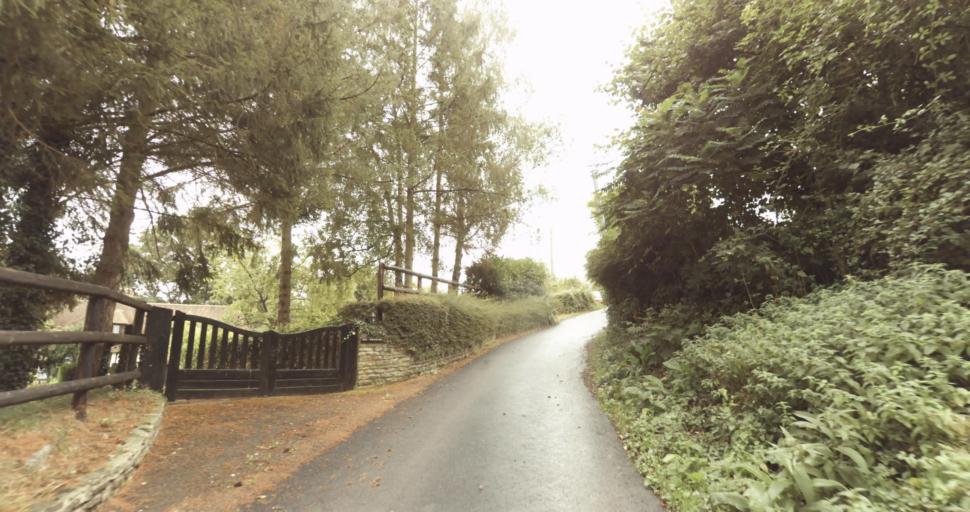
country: FR
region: Lower Normandy
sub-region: Departement de l'Orne
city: Vimoutiers
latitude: 48.8722
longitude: 0.2200
